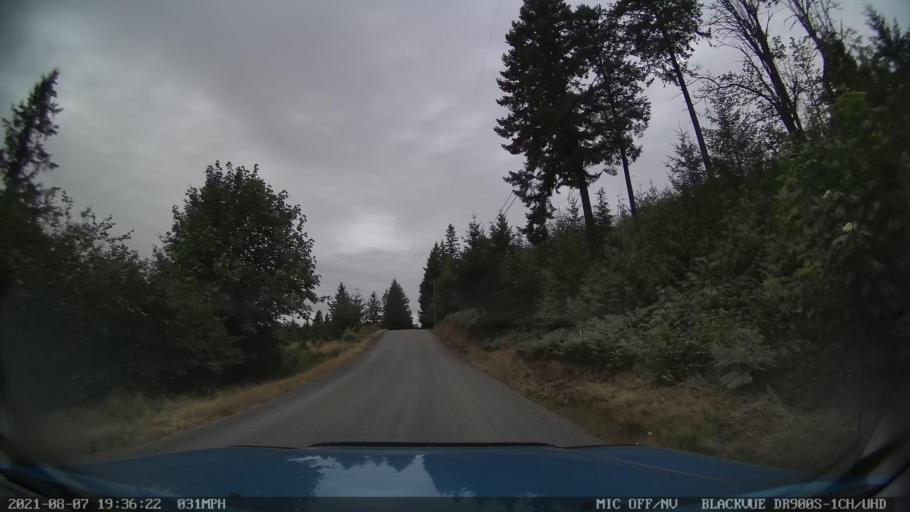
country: US
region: Oregon
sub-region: Marion County
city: Silverton
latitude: 44.9328
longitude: -122.6567
